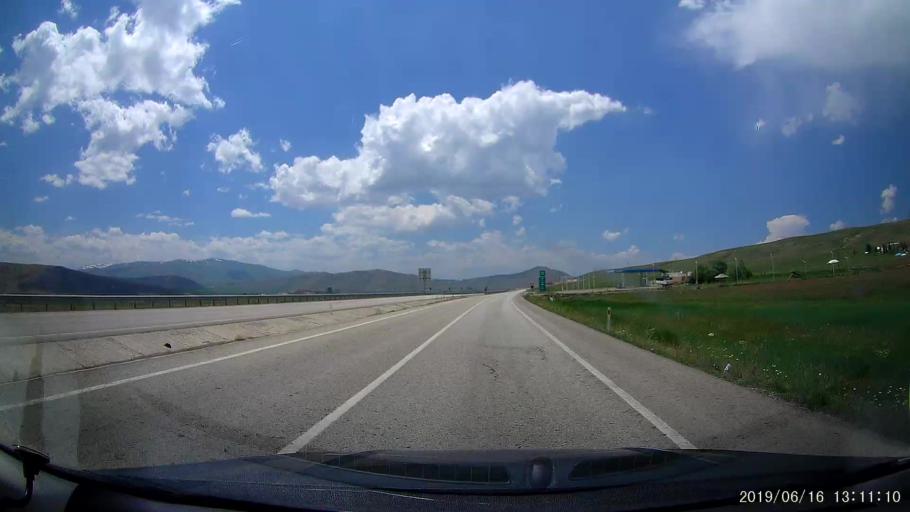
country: TR
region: Agri
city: Diyadin
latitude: 39.5910
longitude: 43.6147
